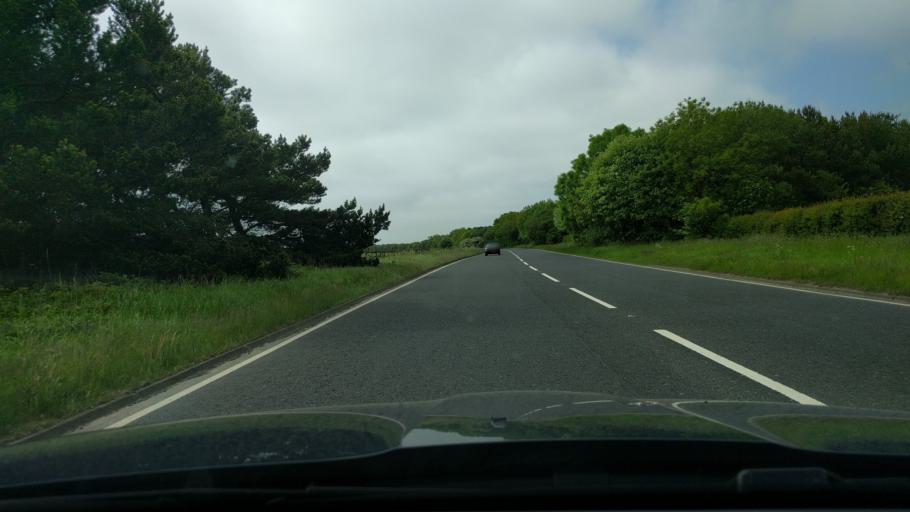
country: GB
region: England
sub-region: Northumberland
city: East Chevington
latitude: 55.2716
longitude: -1.6029
